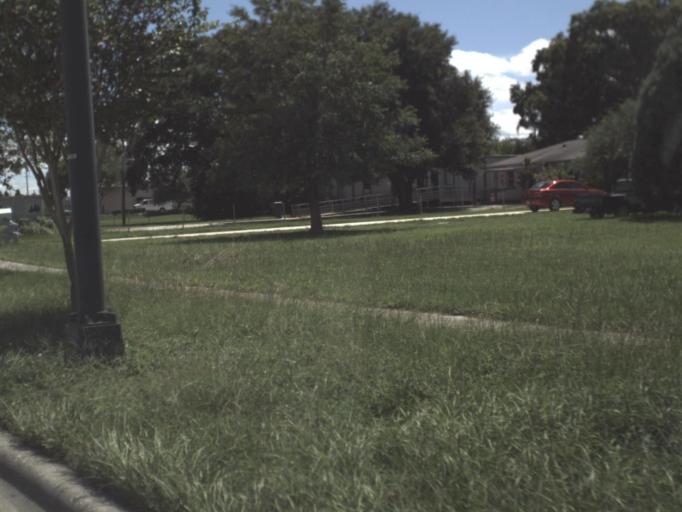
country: US
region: Florida
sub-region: Polk County
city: Lakeland
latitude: 28.0528
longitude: -81.9309
